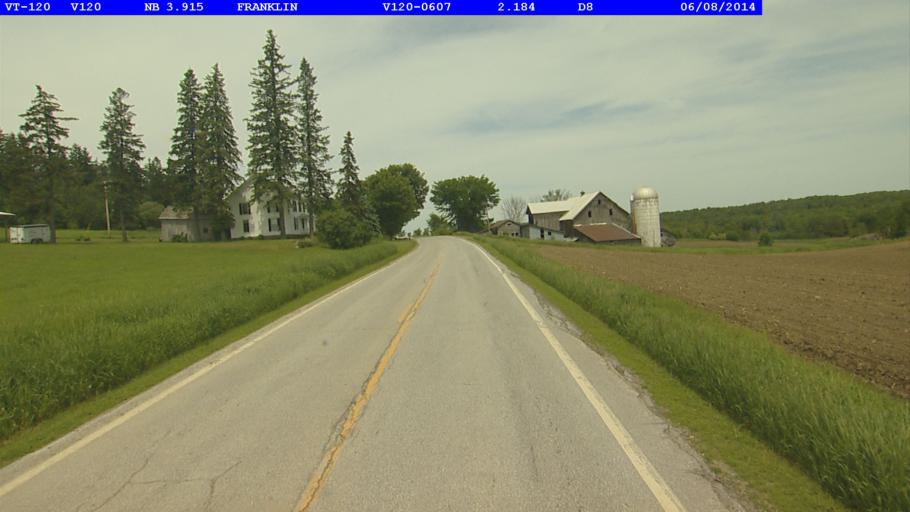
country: US
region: Vermont
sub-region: Franklin County
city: Enosburg Falls
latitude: 44.9644
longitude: -72.9072
